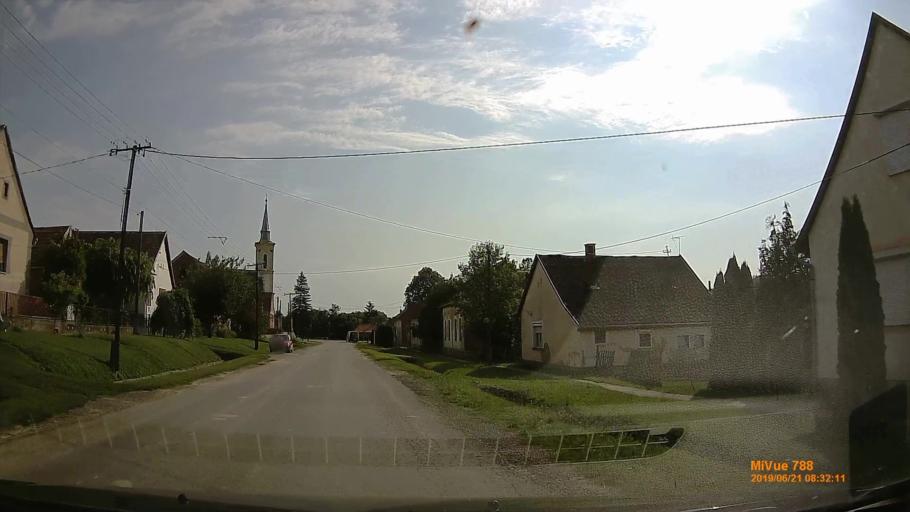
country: HU
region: Baranya
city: Buekkoesd
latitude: 46.1557
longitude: 17.8727
